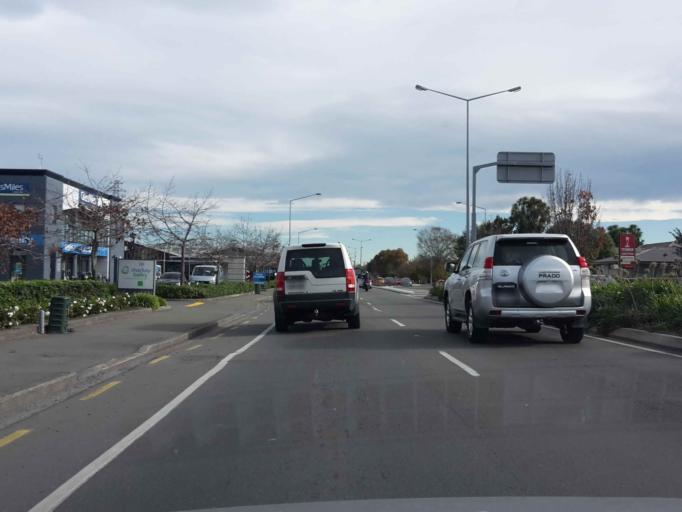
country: NZ
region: Canterbury
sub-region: Christchurch City
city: Christchurch
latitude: -43.5371
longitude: 172.6021
